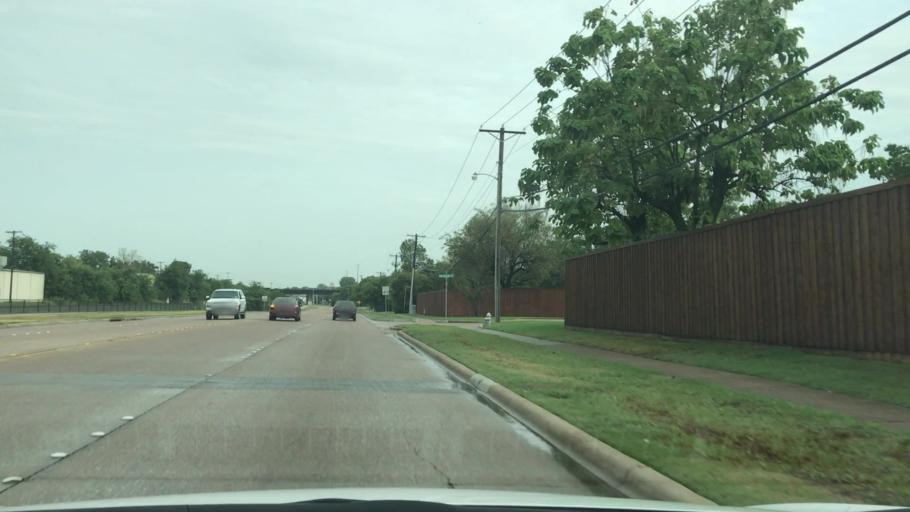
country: US
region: Texas
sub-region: Denton County
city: Lewisville
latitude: 33.0634
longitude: -97.0046
